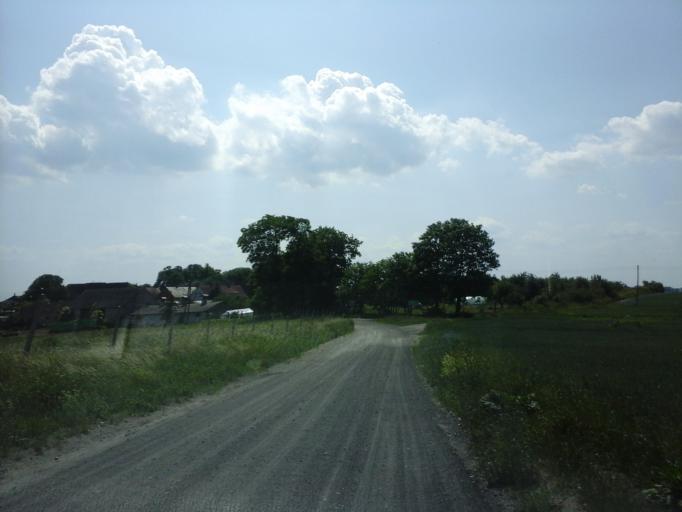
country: PL
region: West Pomeranian Voivodeship
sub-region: Powiat choszczenski
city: Choszczno
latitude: 53.1487
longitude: 15.4071
